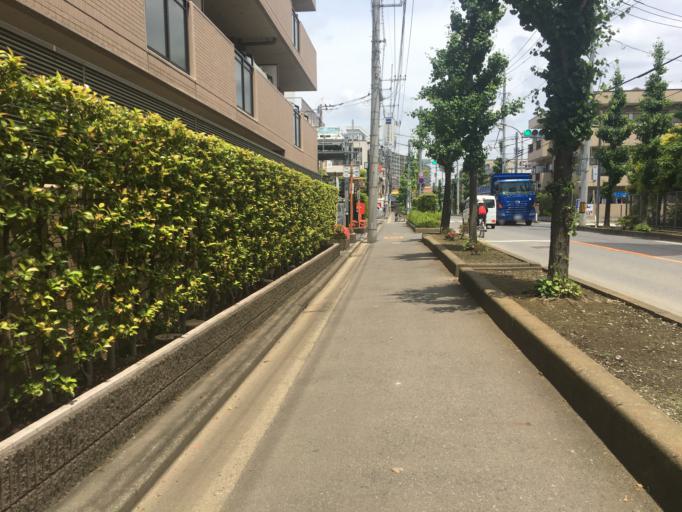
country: JP
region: Saitama
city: Shimotoda
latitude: 35.8047
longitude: 139.6863
